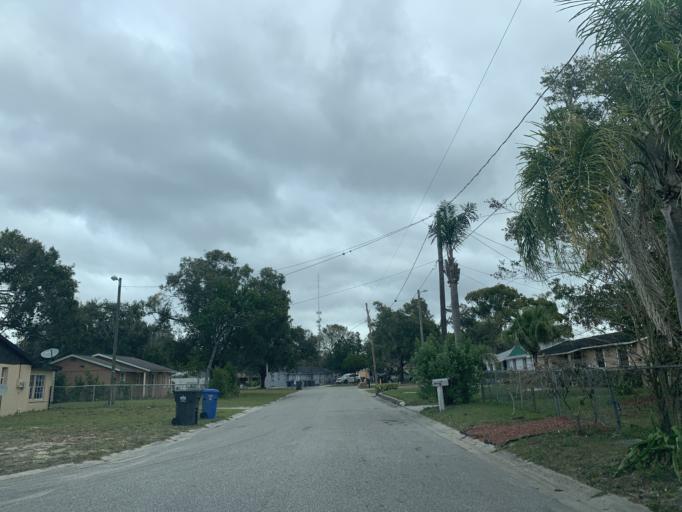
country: US
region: Florida
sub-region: Hillsborough County
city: East Lake-Orient Park
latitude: 27.9762
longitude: -82.3924
